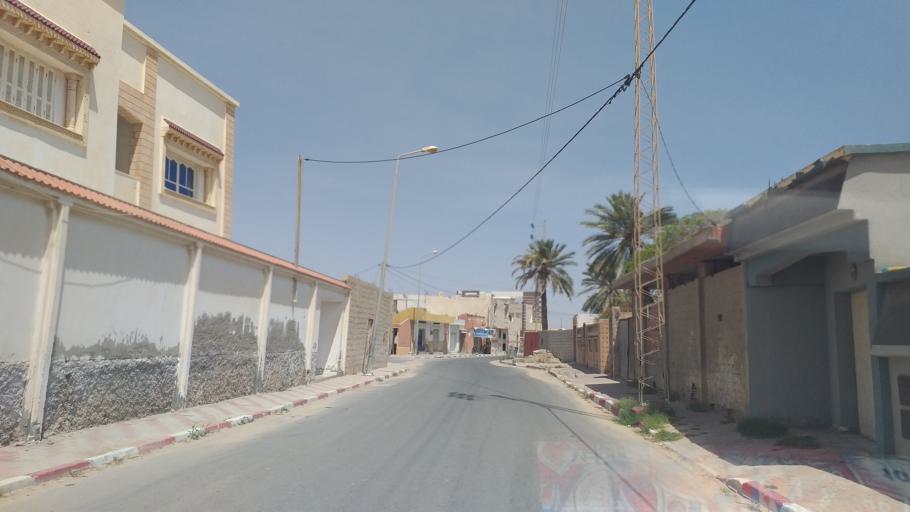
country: TN
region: Qabis
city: Gabes
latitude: 33.9443
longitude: 10.0623
